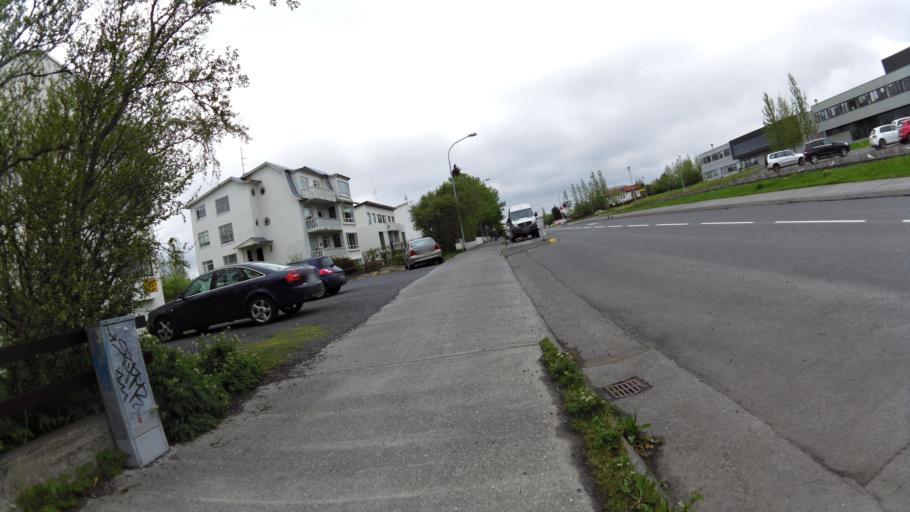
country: IS
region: Capital Region
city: Reykjavik
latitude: 64.1311
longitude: -21.9059
